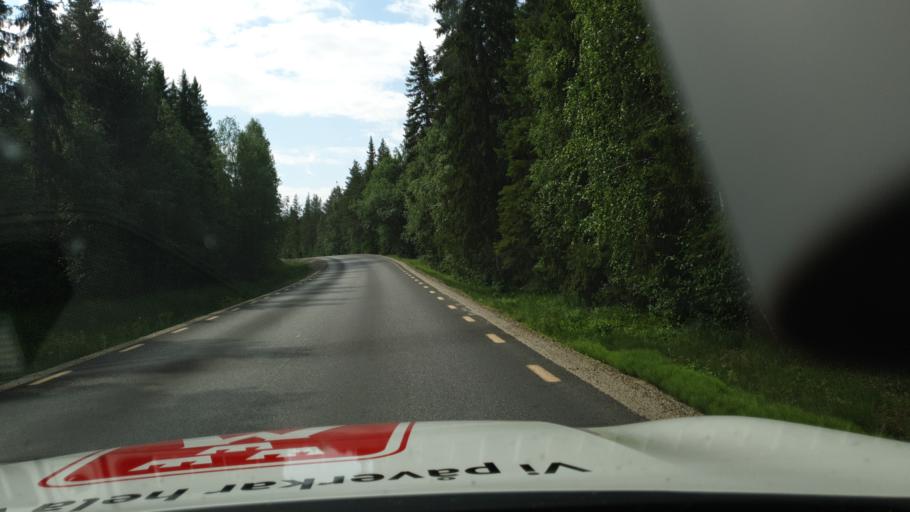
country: SE
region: Vaesterbotten
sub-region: Norsjo Kommun
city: Norsjoe
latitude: 64.4678
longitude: 19.3275
